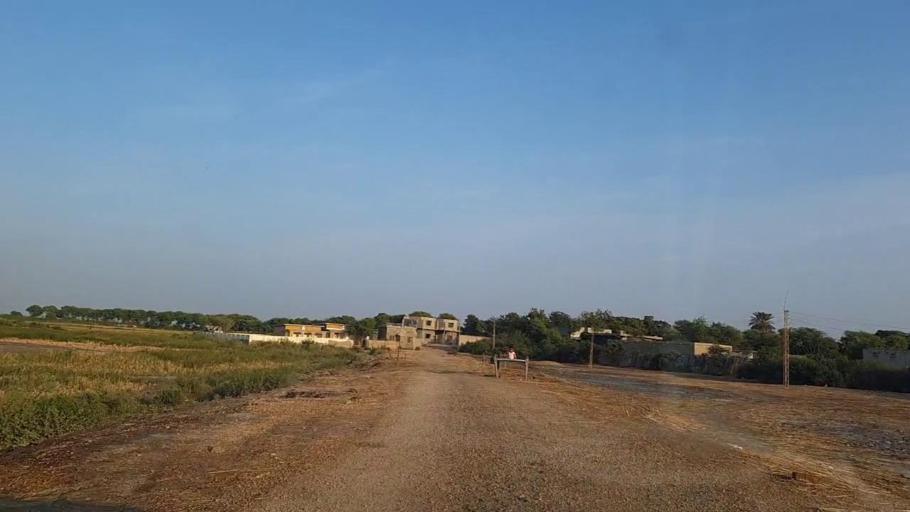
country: PK
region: Sindh
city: Daro Mehar
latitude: 24.6138
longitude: 68.0949
